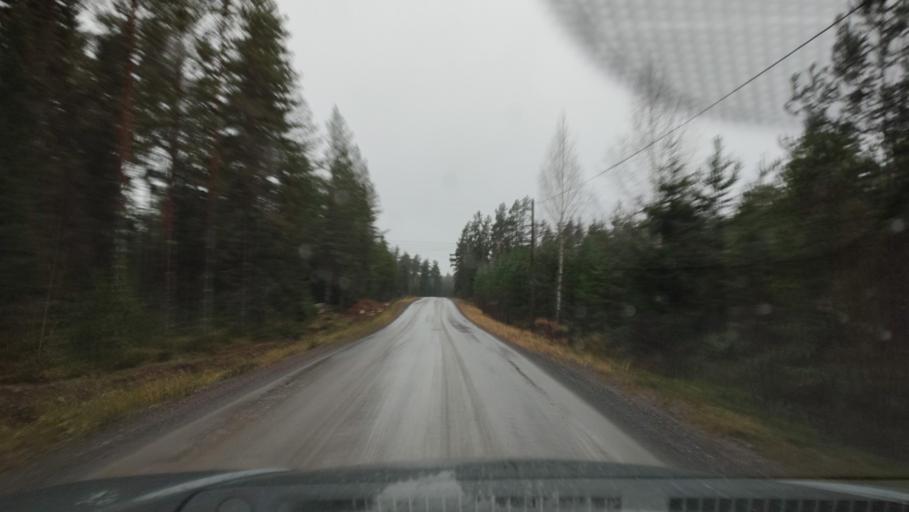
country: FI
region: Southern Ostrobothnia
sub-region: Suupohja
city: Karijoki
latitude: 62.1366
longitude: 21.6691
